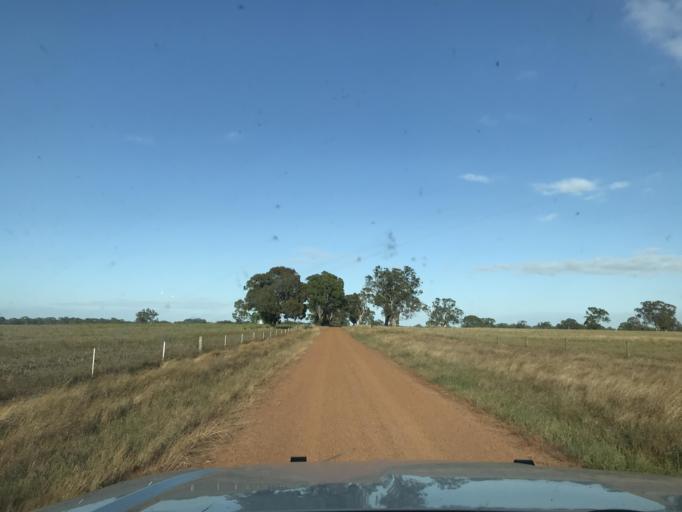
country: AU
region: South Australia
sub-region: Naracoorte and Lucindale
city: Naracoorte
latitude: -36.9562
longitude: 141.3728
